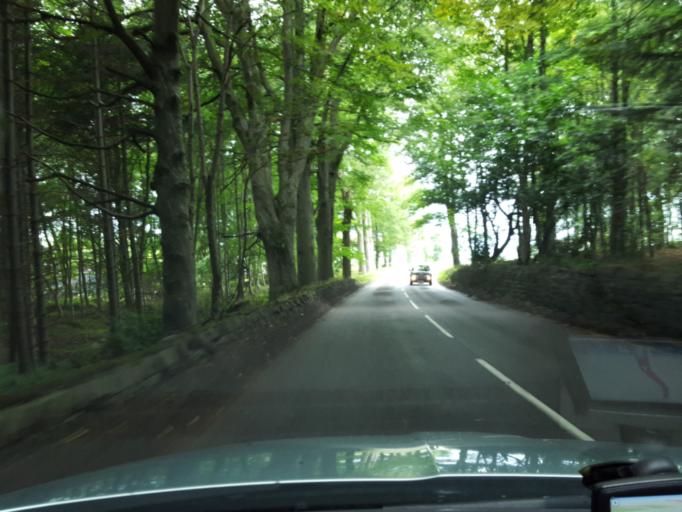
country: GB
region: Scotland
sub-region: Aberdeenshire
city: Kemnay
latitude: 57.1650
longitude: -2.4252
